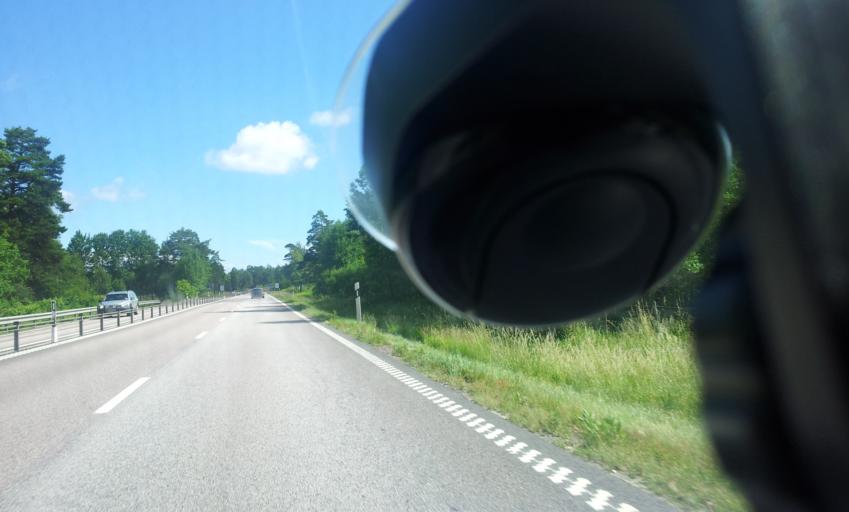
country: SE
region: Kalmar
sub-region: Monsteras Kommun
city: Moensteras
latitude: 57.0729
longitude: 16.4756
